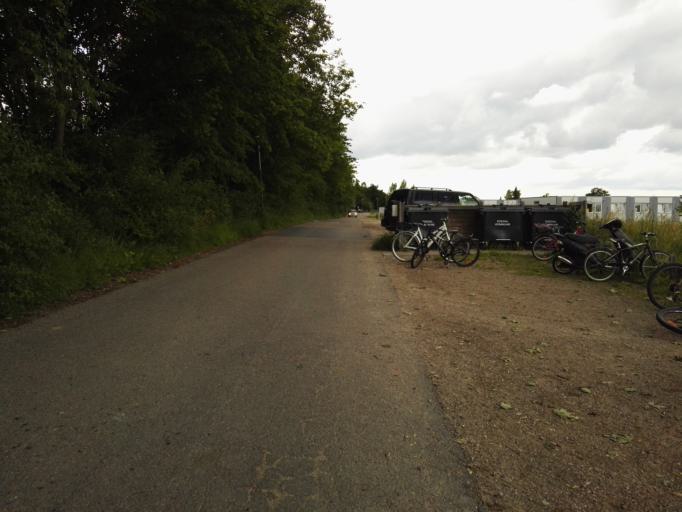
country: DK
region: Capital Region
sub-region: Egedal Kommune
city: Stenlose
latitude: 55.7620
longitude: 12.2001
